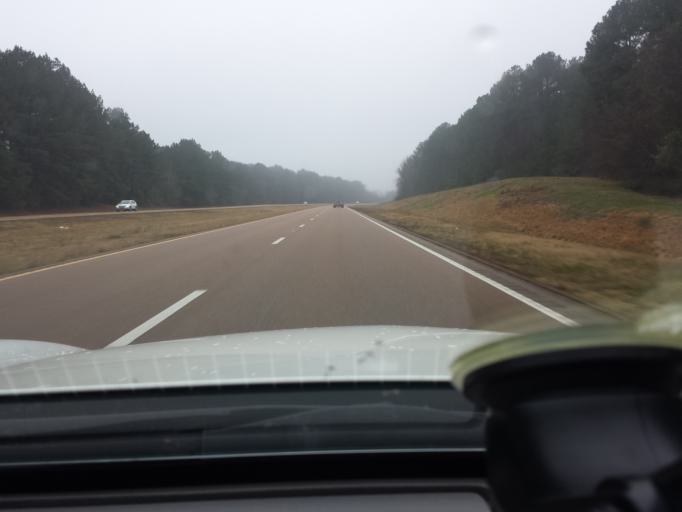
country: US
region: Mississippi
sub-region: Leake County
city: Carthage
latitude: 32.6496
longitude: -89.6523
